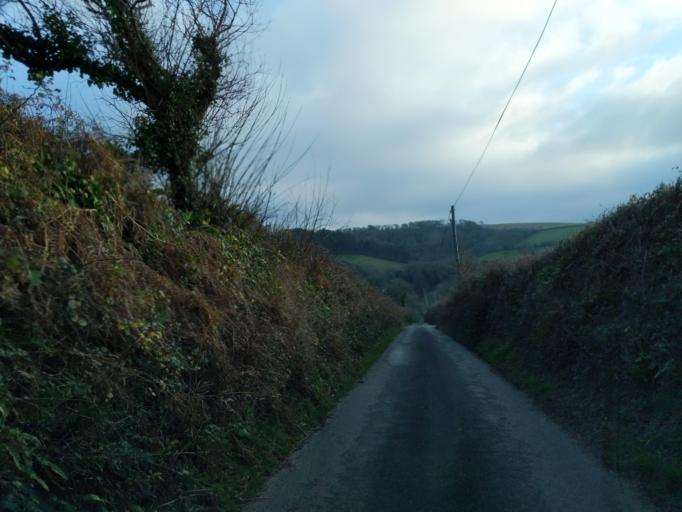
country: GB
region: England
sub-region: Cornwall
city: Pillaton
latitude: 50.3921
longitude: -4.3266
